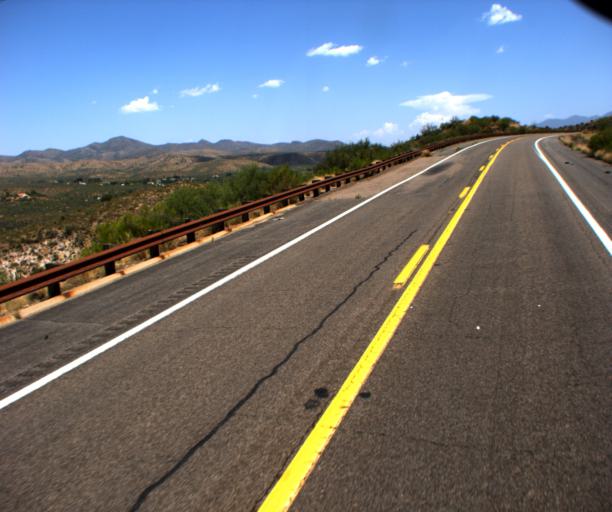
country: US
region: Arizona
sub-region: Gila County
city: Claypool
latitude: 33.5072
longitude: -110.8685
